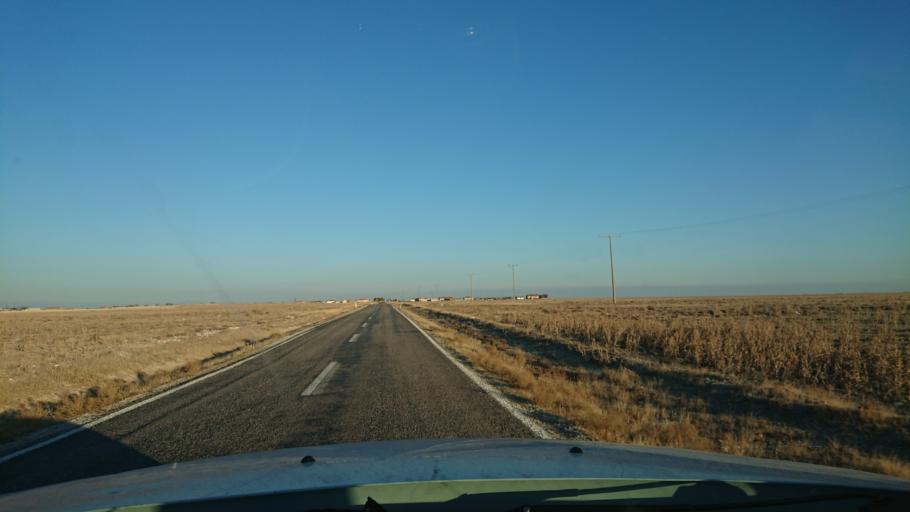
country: TR
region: Aksaray
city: Eskil
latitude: 38.4641
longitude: 33.2379
